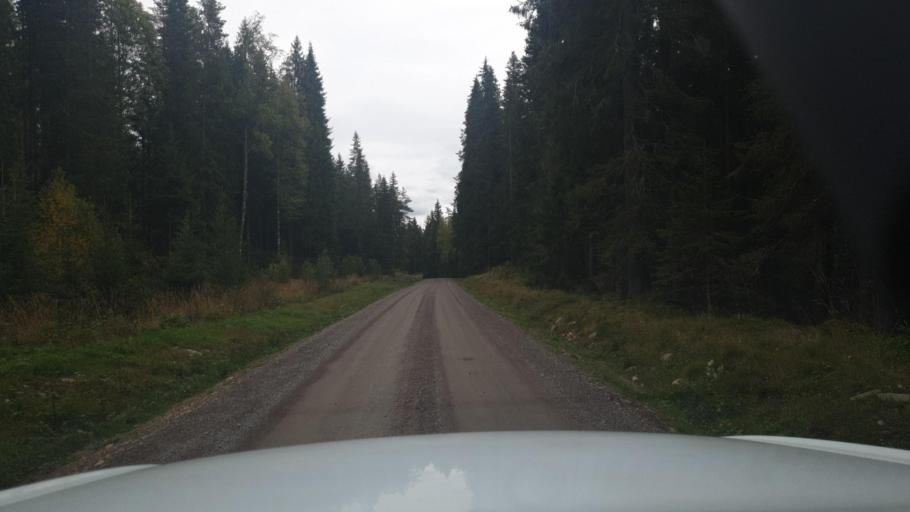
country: SE
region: Vaermland
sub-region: Eda Kommun
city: Charlottenberg
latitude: 60.0373
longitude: 12.5899
